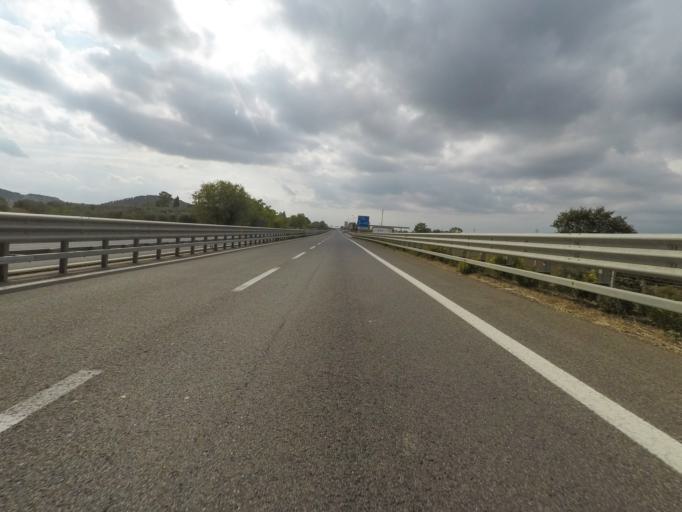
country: IT
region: Tuscany
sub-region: Provincia di Grosseto
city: Bagno Roselle
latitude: 42.8296
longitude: 11.1404
